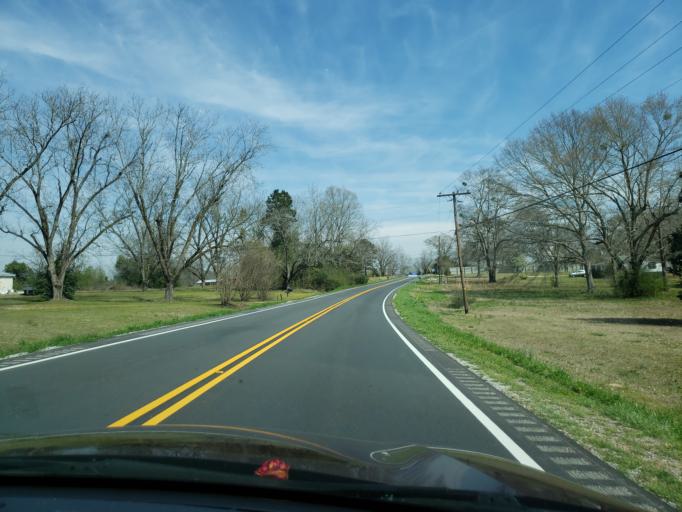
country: US
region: Alabama
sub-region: Elmore County
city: Tallassee
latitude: 32.5802
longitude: -85.7542
